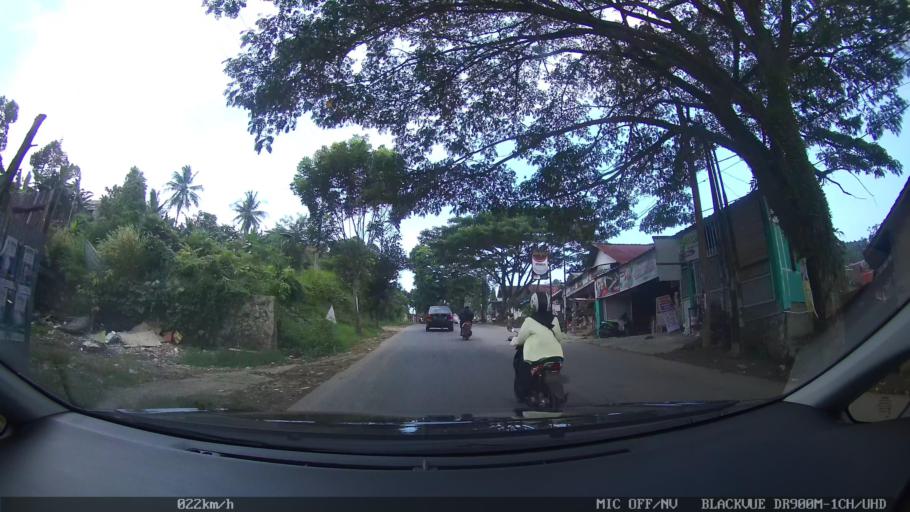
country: ID
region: Lampung
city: Bandarlampung
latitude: -5.4072
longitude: 105.2196
